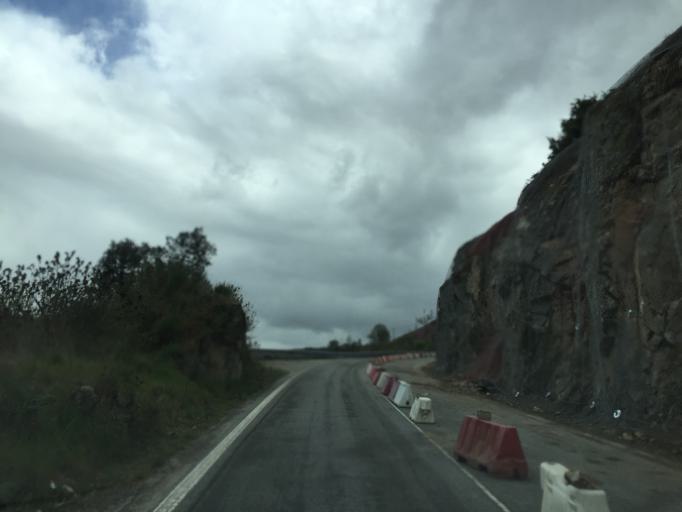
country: PT
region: Braganca
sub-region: Miranda do Douro
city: Miranda do Douro
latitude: 41.4934
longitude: -6.2704
